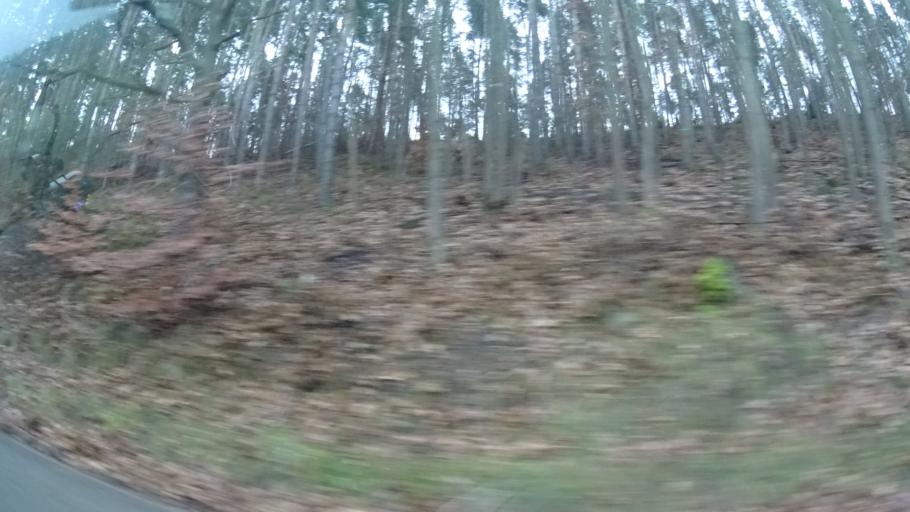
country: DE
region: Thuringia
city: Rausdorf
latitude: 50.8601
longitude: 11.6917
